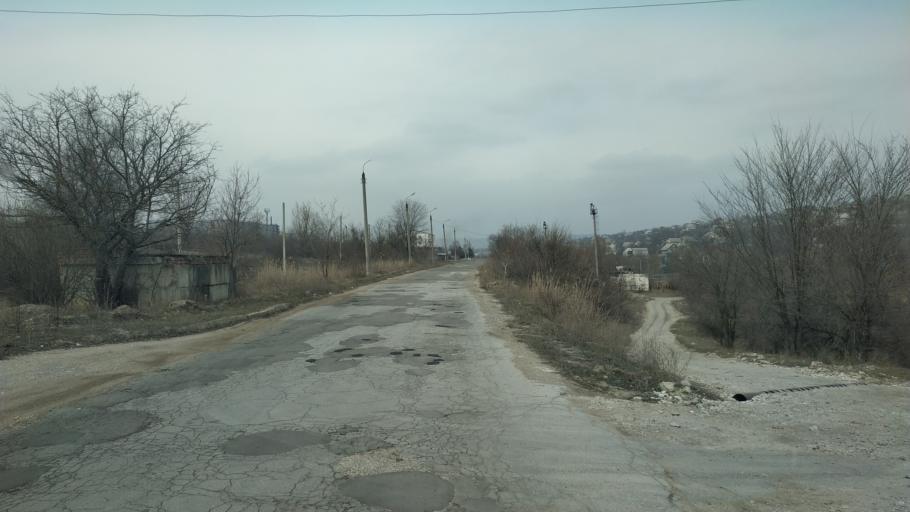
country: MD
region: Chisinau
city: Singera
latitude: 46.9056
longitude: 29.0181
